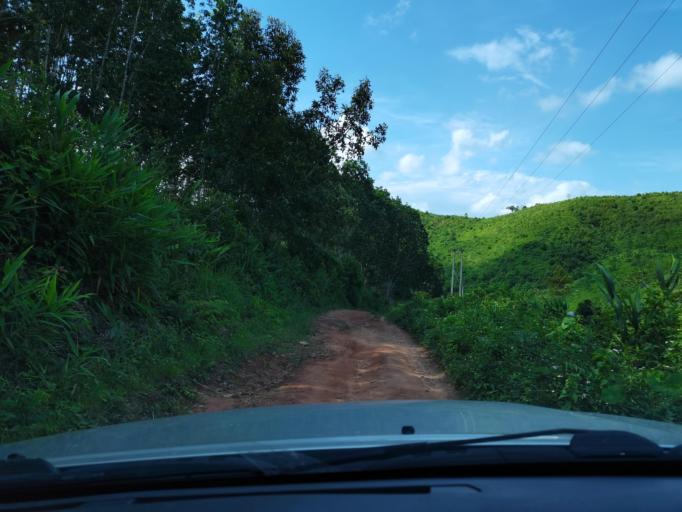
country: LA
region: Loungnamtha
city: Muang Nale
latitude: 20.5664
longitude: 101.0575
